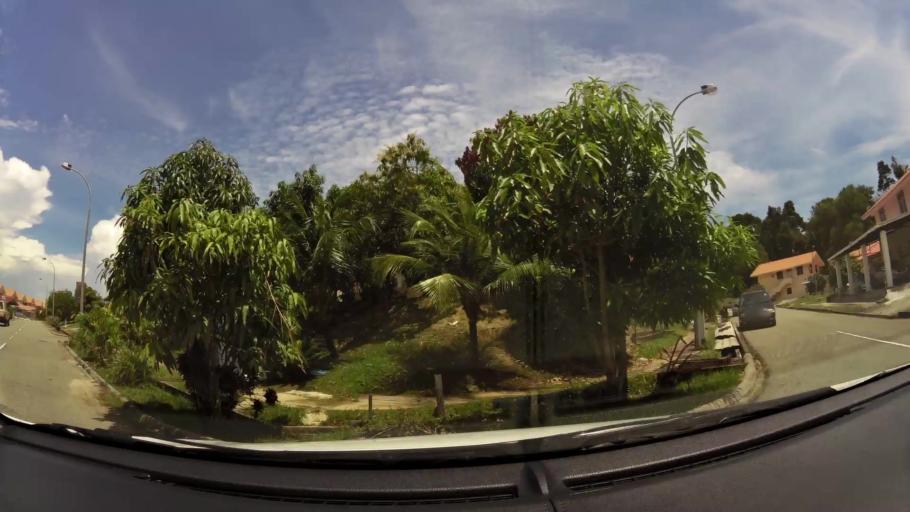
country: BN
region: Brunei and Muara
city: Bandar Seri Begawan
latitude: 4.9647
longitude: 114.9105
